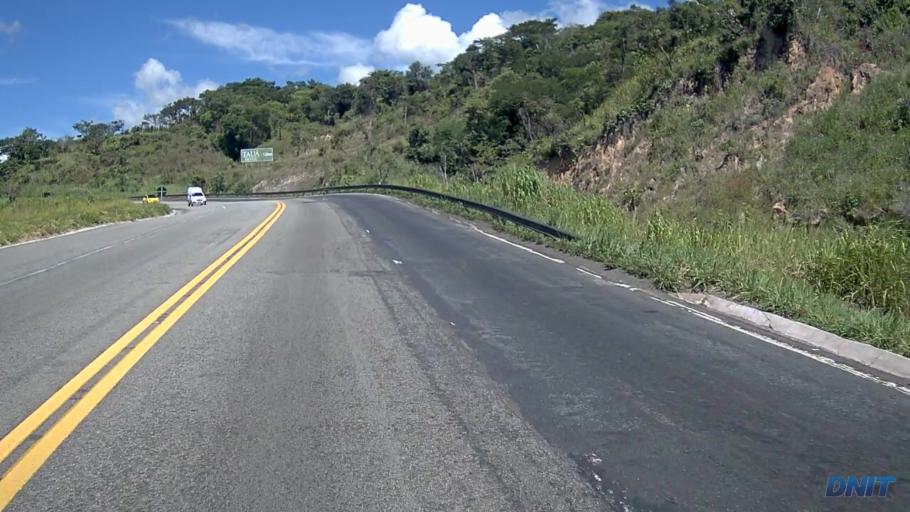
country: BR
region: Minas Gerais
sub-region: Caete
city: Caete
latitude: -19.7874
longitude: -43.7282
